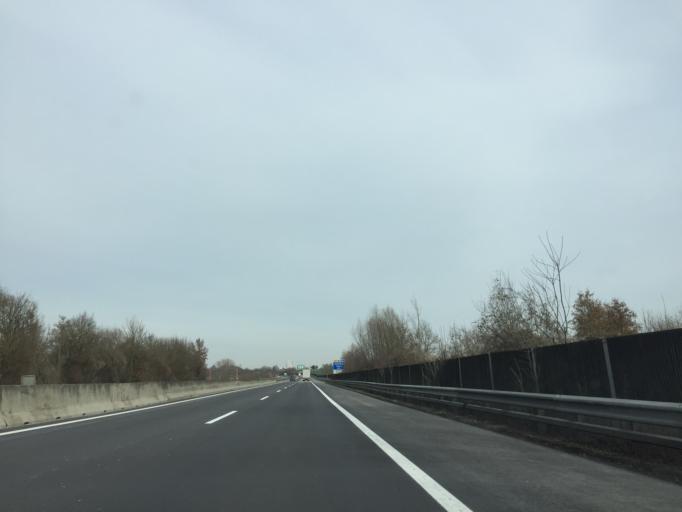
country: AT
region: Upper Austria
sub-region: Politischer Bezirk Scharding
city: Sankt Marienkirchen bei Schaerding
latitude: 48.3814
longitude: 13.4189
